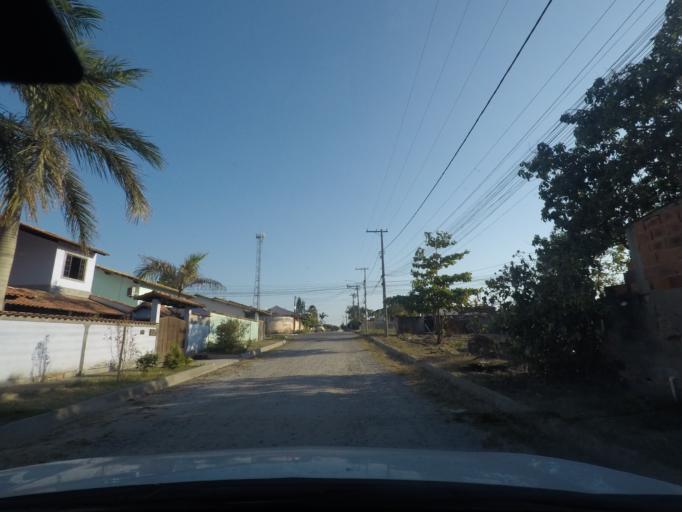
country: BR
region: Rio de Janeiro
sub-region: Marica
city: Marica
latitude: -22.9666
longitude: -42.9343
